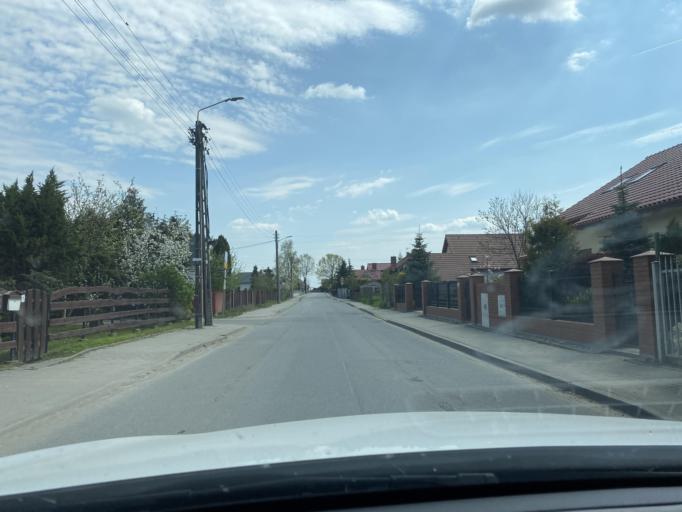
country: PL
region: Lower Silesian Voivodeship
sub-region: Powiat wroclawski
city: Mirkow
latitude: 51.1606
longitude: 17.1702
